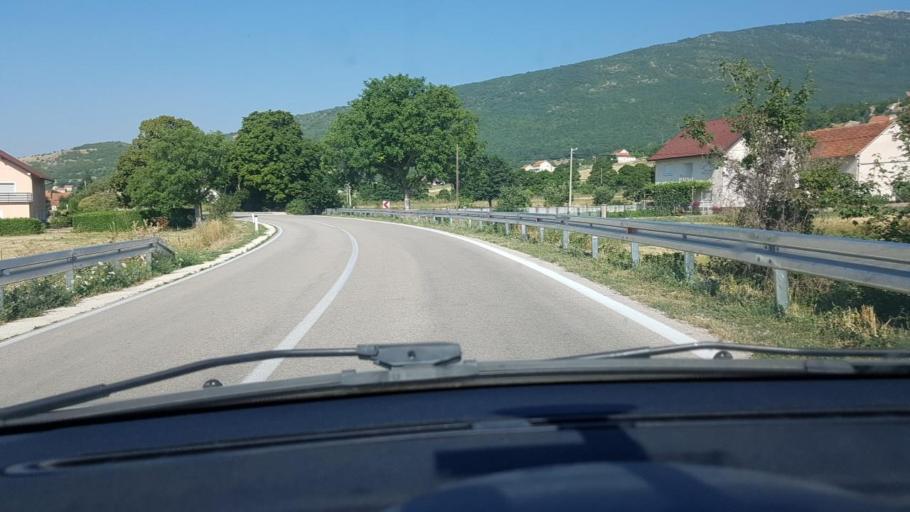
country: BA
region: Federation of Bosnia and Herzegovina
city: Zabrisce
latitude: 43.8703
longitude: 16.9225
